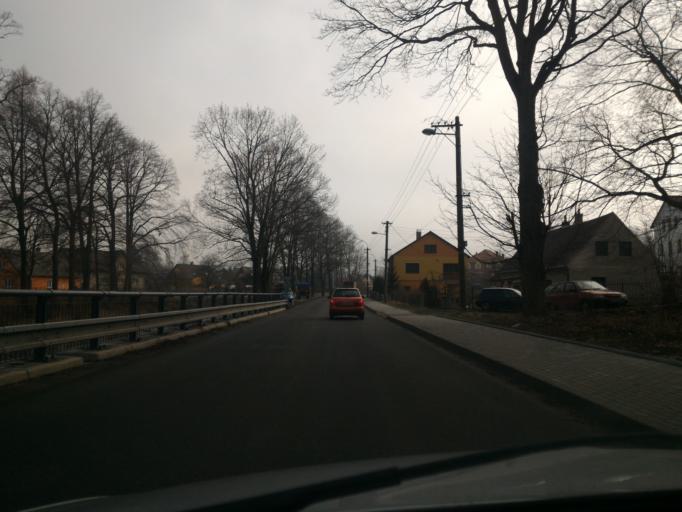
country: CZ
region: Liberecky
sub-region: Okres Liberec
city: Raspenava
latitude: 50.9010
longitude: 15.1254
